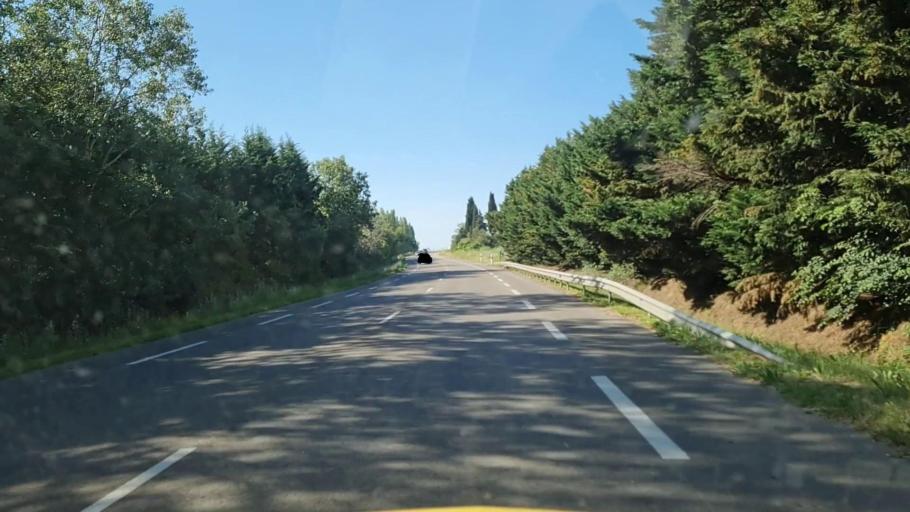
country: FR
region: Languedoc-Roussillon
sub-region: Departement du Gard
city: Garons
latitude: 43.7348
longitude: 4.4100
